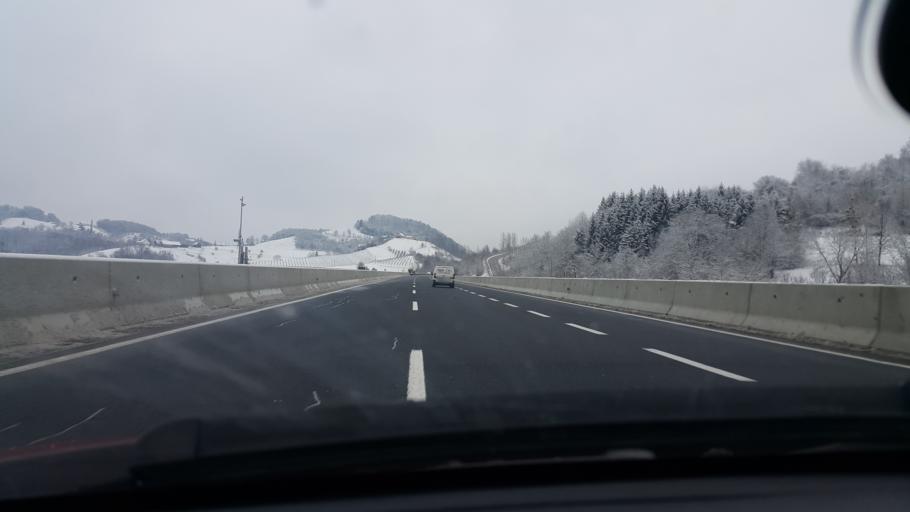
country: SI
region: Sentilj
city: Sentilj v Slov. Goricah
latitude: 46.6605
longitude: 15.6465
